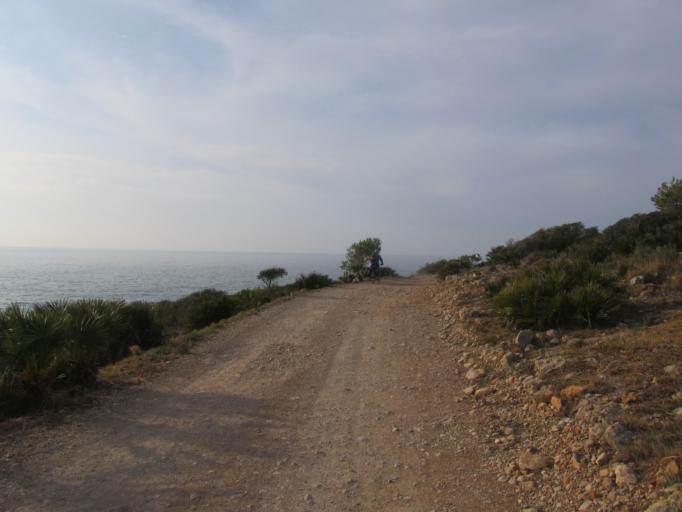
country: ES
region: Valencia
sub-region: Provincia de Castello
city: Peniscola
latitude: 40.3177
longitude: 0.3595
